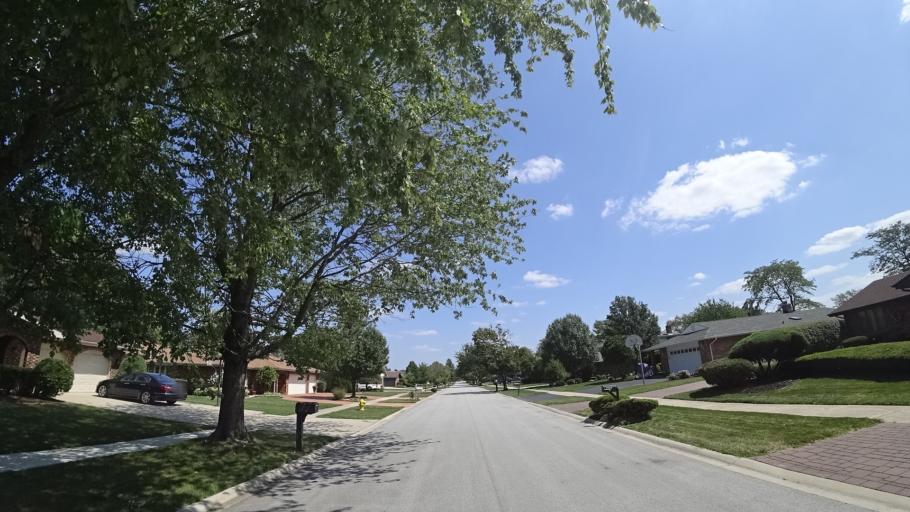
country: US
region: Illinois
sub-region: Cook County
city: Orland Park
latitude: 41.6260
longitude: -87.8306
